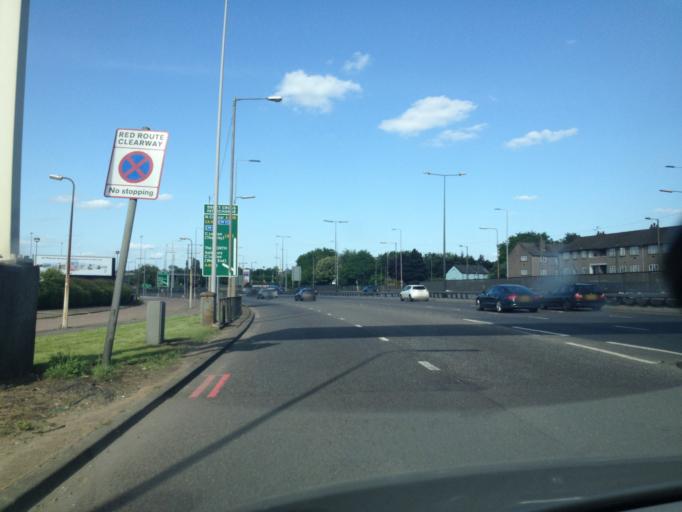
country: GB
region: England
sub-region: Greater London
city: Hendon
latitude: 51.5736
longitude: -0.2231
